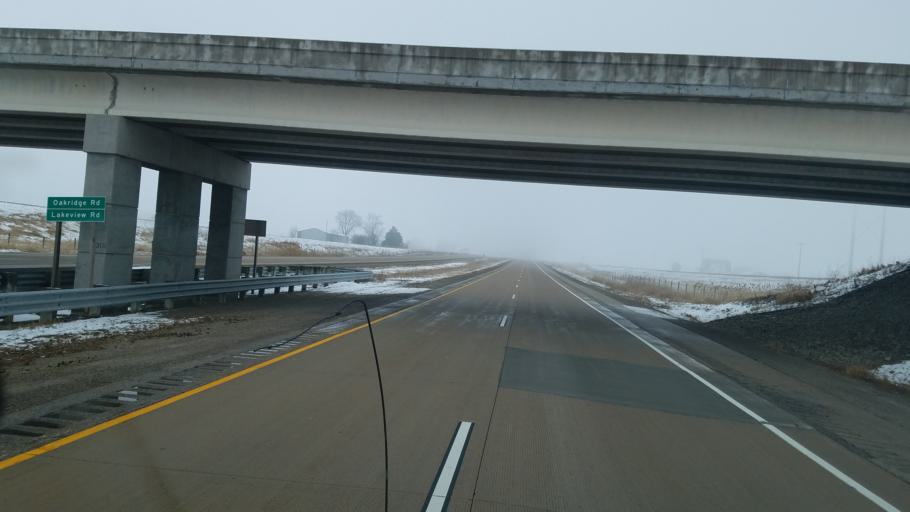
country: US
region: Wisconsin
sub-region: Winnebago County
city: Winneconne
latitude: 44.1693
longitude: -88.6643
